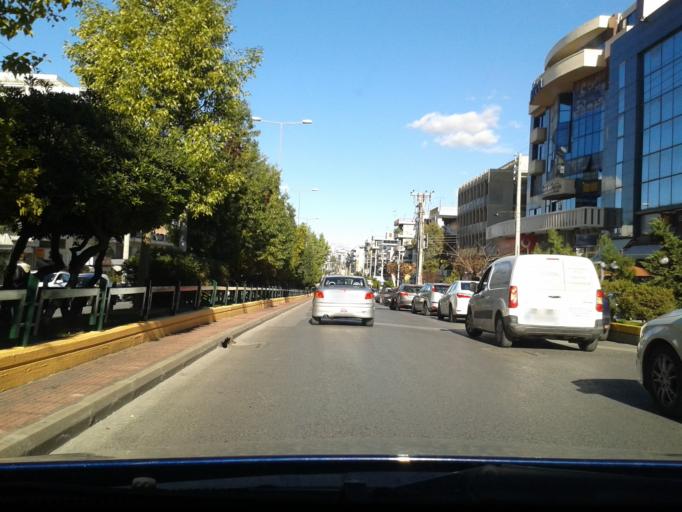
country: GR
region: Attica
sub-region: Nomarchia Athinas
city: Galatsi
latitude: 38.0138
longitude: 23.7538
